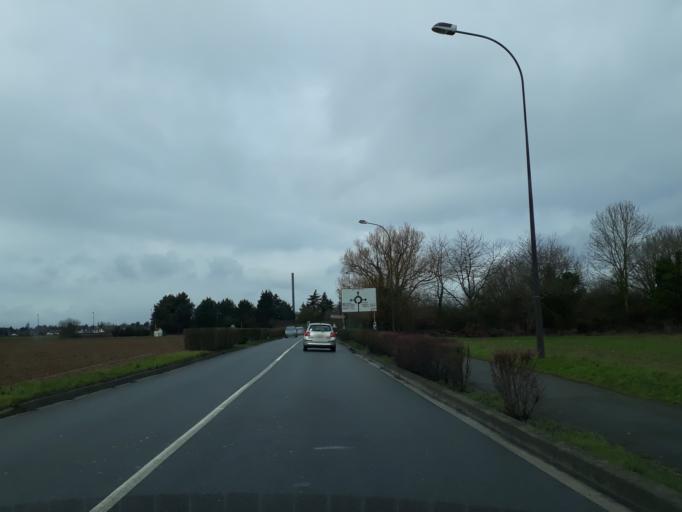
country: FR
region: Ile-de-France
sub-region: Departement de l'Essonne
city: Gometz-le-Chatel
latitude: 48.6745
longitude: 2.1350
